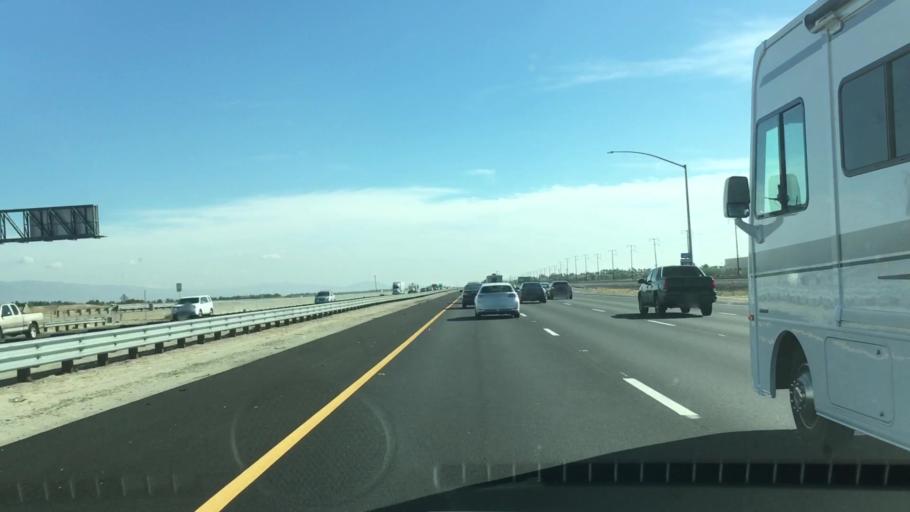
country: US
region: California
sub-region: Riverside County
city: Thousand Palms
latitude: 33.7835
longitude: -116.3506
